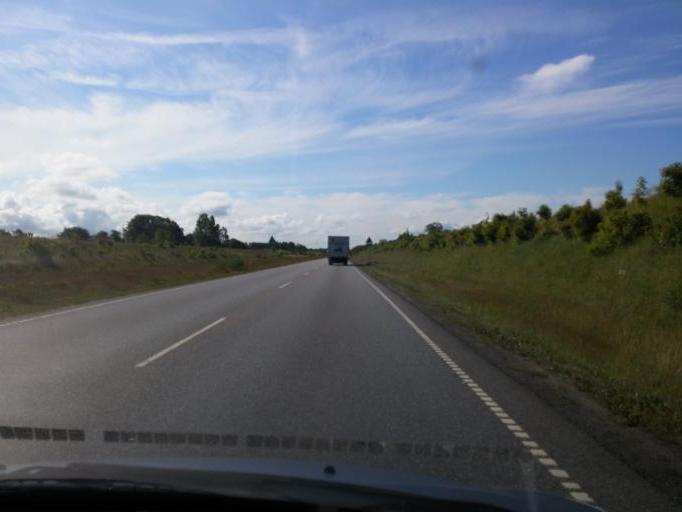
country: DK
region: South Denmark
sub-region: Odense Kommune
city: Bullerup
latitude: 55.4241
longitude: 10.4626
